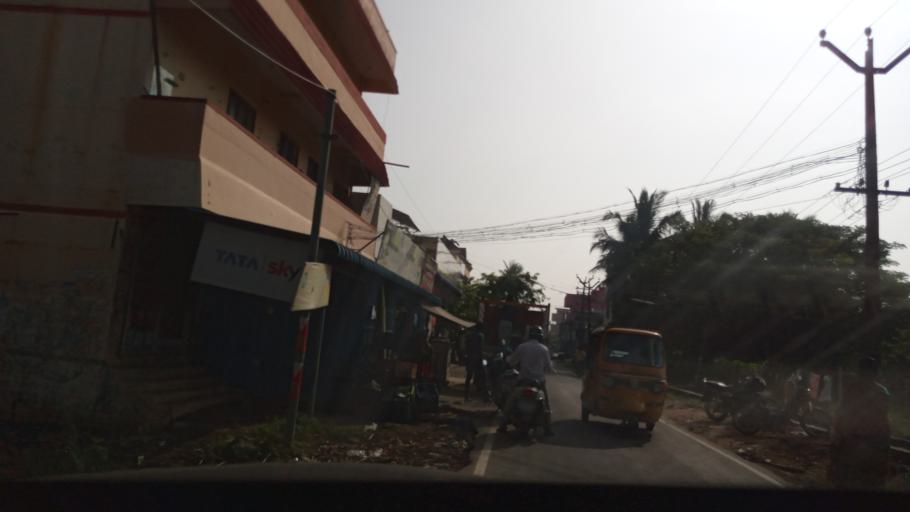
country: IN
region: Tamil Nadu
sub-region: Kancheepuram
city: Guduvancheri
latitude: 12.8521
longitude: 80.0681
